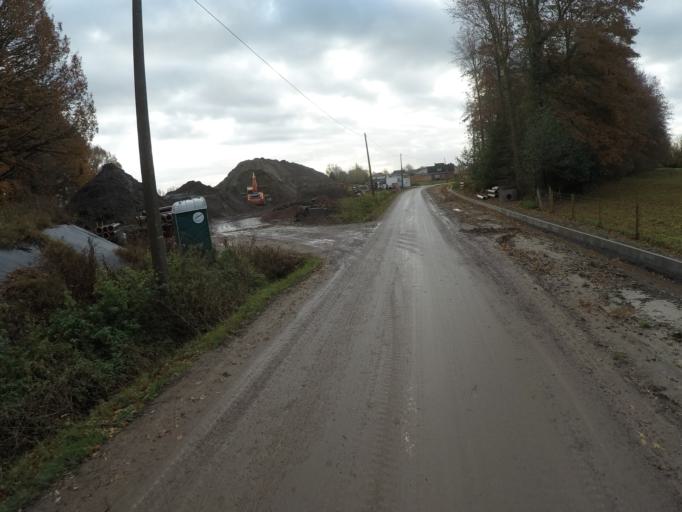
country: BE
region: Flanders
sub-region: Provincie Vlaams-Brabant
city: Londerzeel
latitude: 51.0066
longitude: 4.2843
